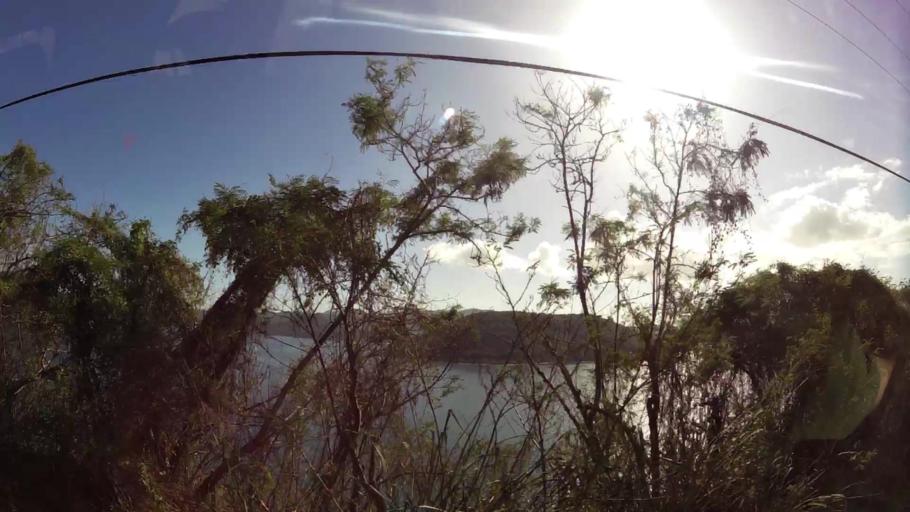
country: VG
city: Road Town
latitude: 18.3883
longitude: -64.7096
